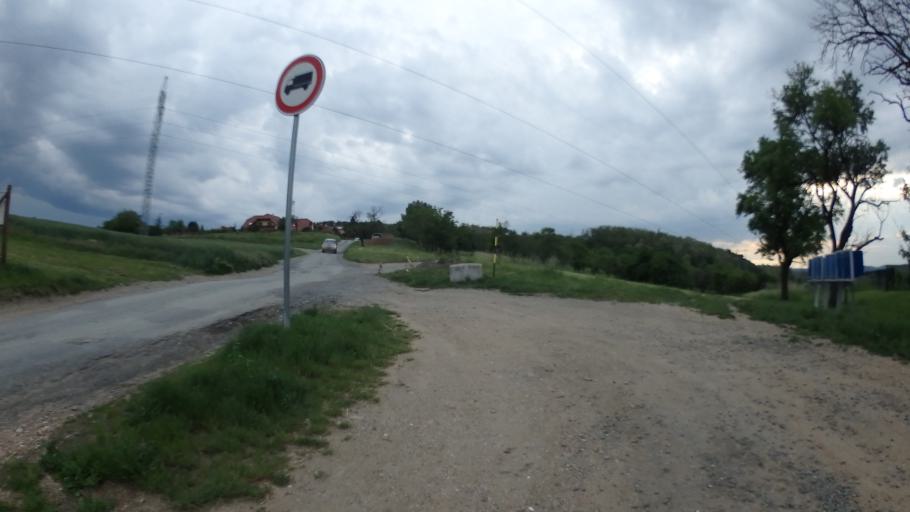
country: CZ
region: South Moravian
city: Ostopovice
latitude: 49.1388
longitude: 16.5512
